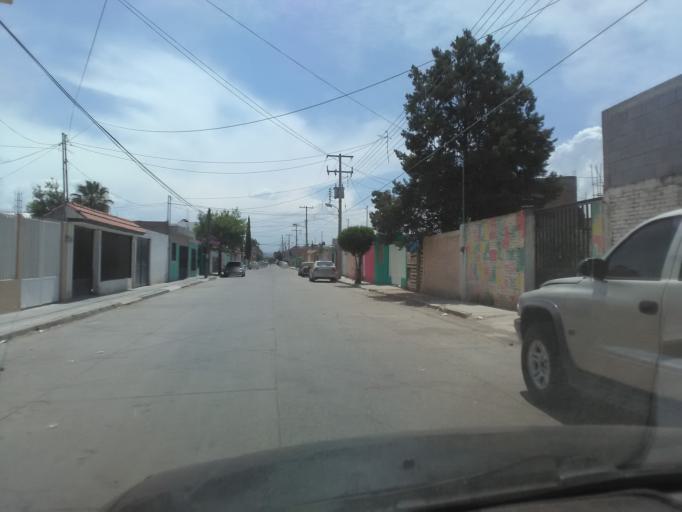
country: MX
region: Durango
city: Victoria de Durango
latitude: 24.0085
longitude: -104.6285
